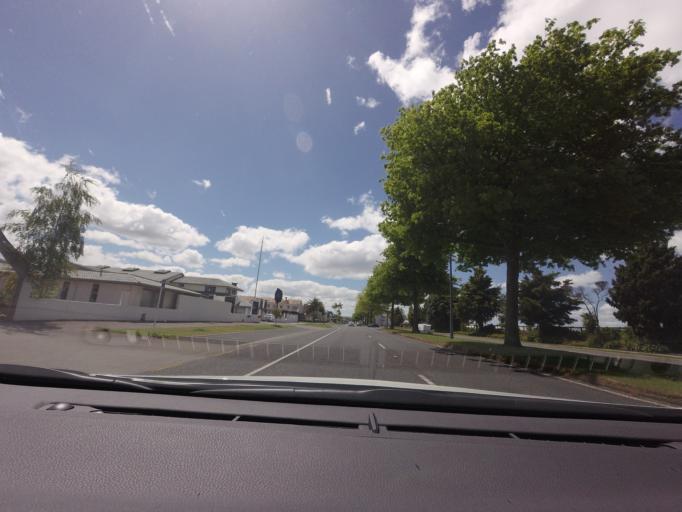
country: NZ
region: Bay of Plenty
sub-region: Rotorua District
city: Rotorua
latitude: -38.1465
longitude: 176.2537
